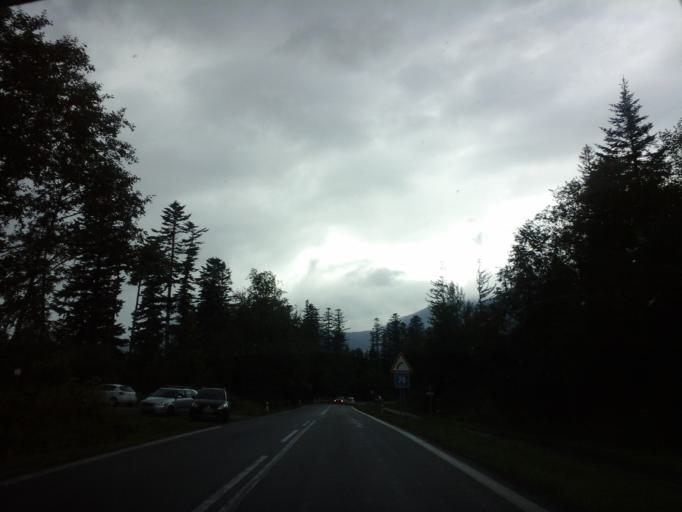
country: SK
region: Presovsky
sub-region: Okres Poprad
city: Zdiar
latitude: 49.2132
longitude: 20.3493
